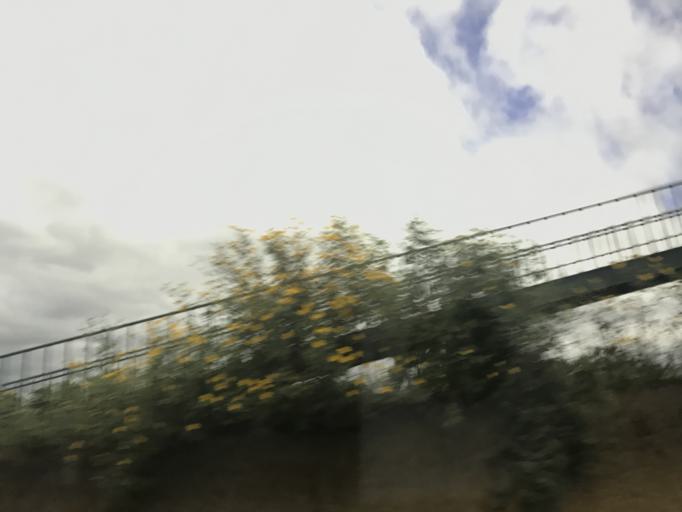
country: GT
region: Chimaltenango
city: Parramos
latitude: 14.6274
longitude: -90.8082
